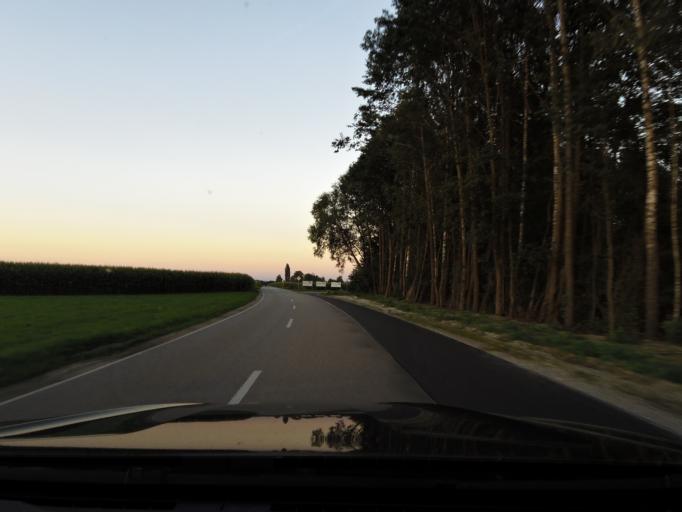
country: DE
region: Bavaria
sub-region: Upper Bavaria
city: Eitting
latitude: 48.3928
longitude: 11.8961
